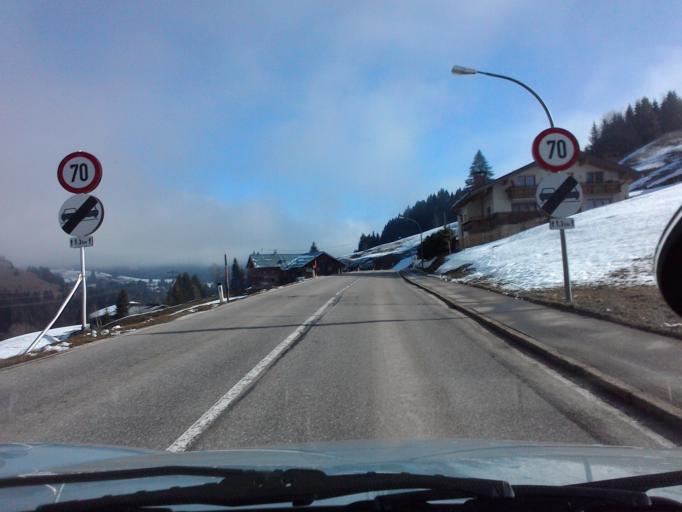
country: AT
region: Vorarlberg
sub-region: Politischer Bezirk Bregenz
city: Mittelberg
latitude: 47.3697
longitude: 10.2032
